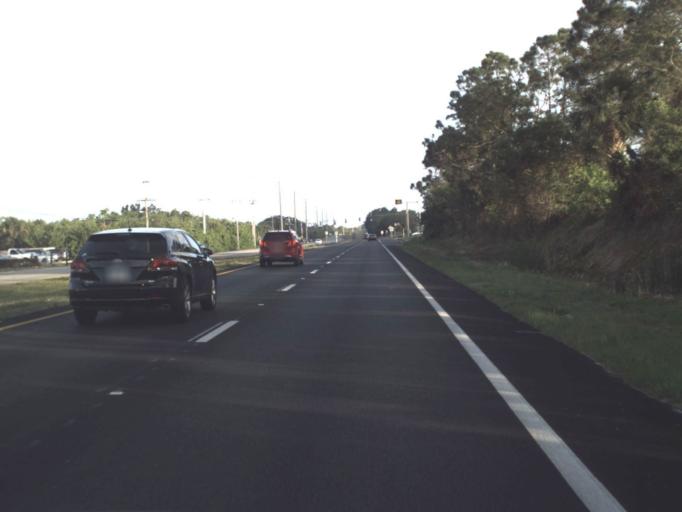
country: US
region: Florida
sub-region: Brevard County
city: South Patrick Shores
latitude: 28.2317
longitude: -80.6741
